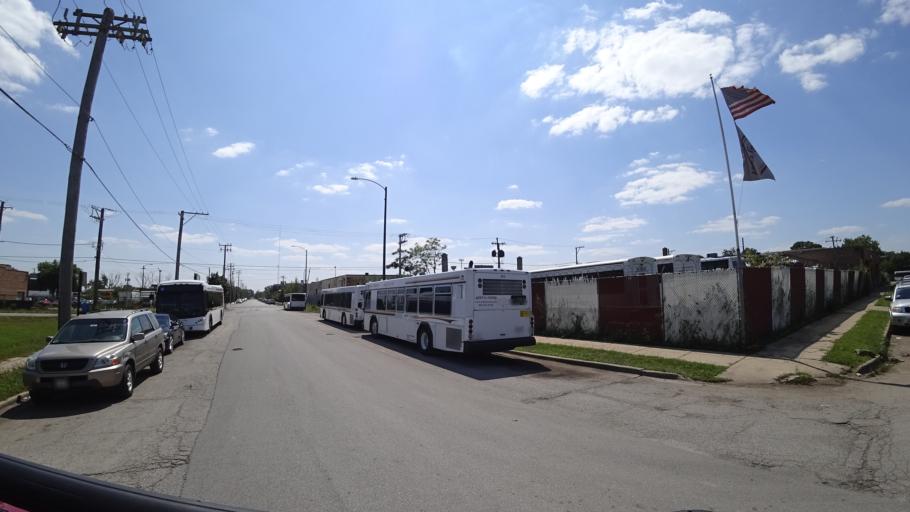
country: US
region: Illinois
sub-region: Cook County
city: Cicero
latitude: 41.8668
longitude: -87.7374
